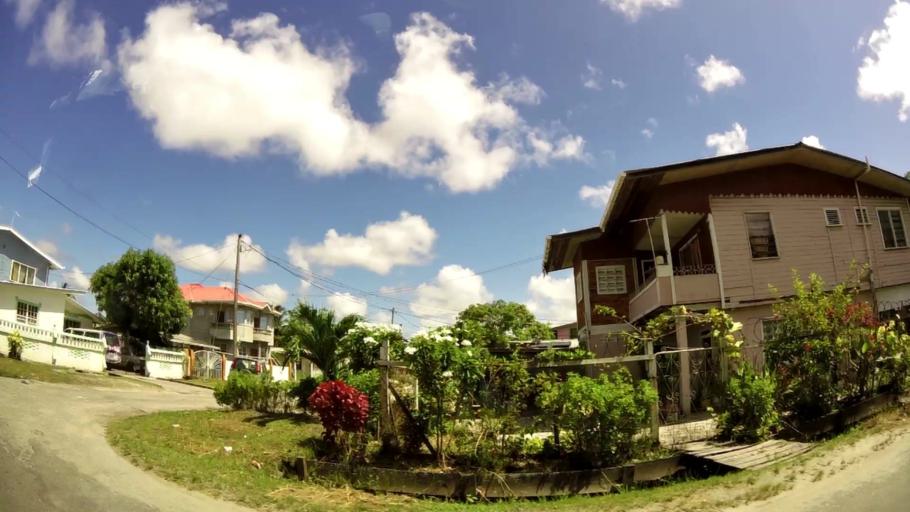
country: GY
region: Demerara-Mahaica
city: Georgetown
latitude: 6.7959
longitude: -58.1406
